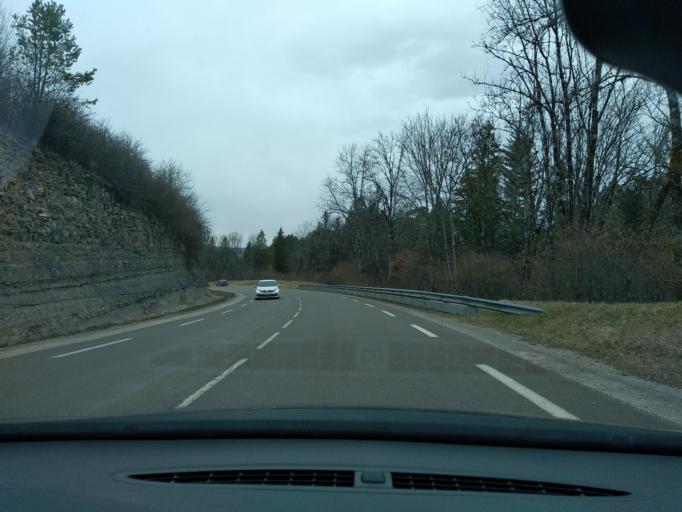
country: FR
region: Franche-Comte
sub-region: Departement du Jura
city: Arinthod
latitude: 46.4067
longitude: 5.5647
